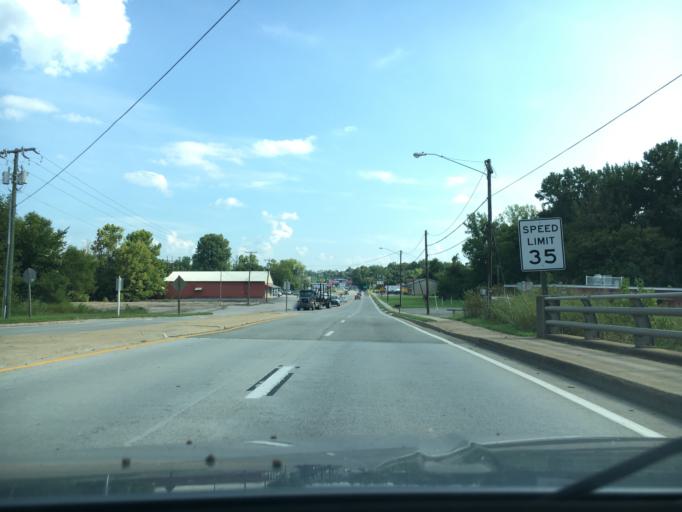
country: US
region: Virginia
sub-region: Halifax County
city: South Boston
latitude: 36.6935
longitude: -78.9006
